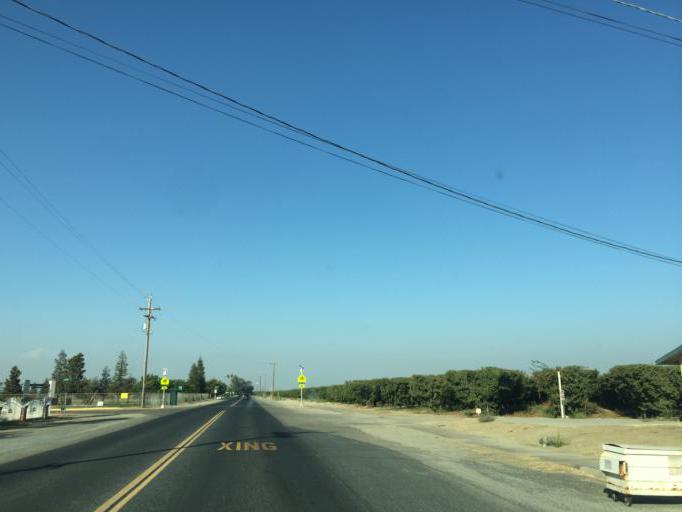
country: US
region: California
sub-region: Tulare County
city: London
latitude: 36.4559
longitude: -119.4822
